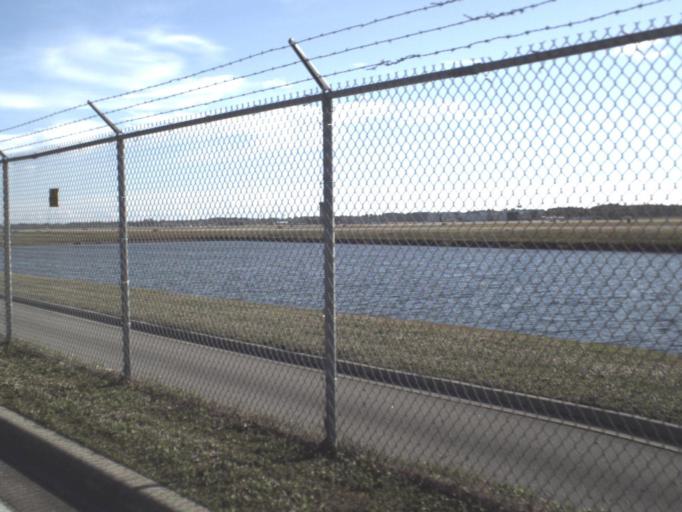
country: US
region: Florida
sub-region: Volusia County
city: Daytona Beach
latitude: 29.1787
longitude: -81.0693
